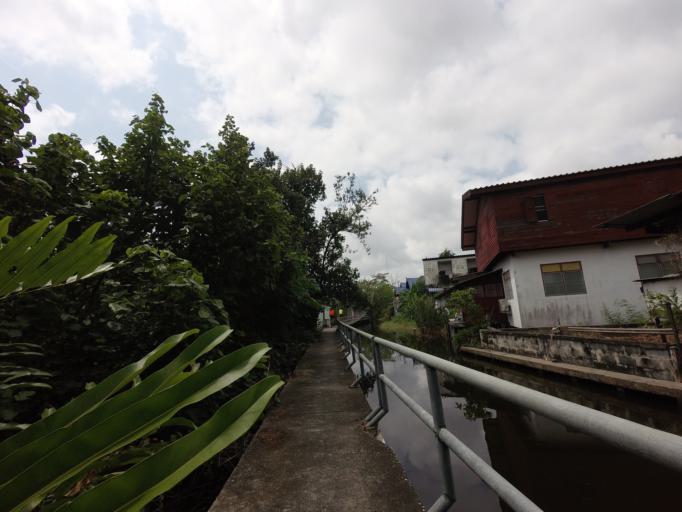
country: TH
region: Bangkok
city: Thung Khru
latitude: 13.6392
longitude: 100.4955
